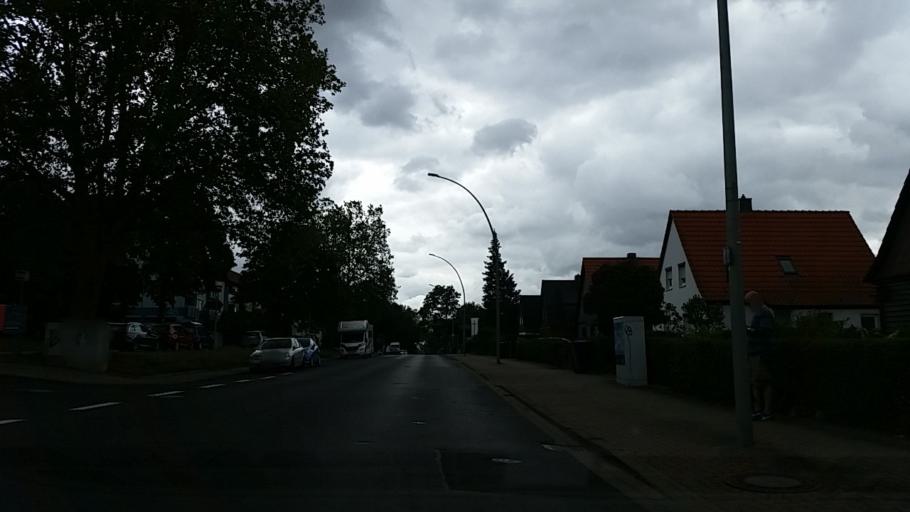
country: DE
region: Lower Saxony
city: Wolfenbuettel
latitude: 52.1559
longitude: 10.5520
